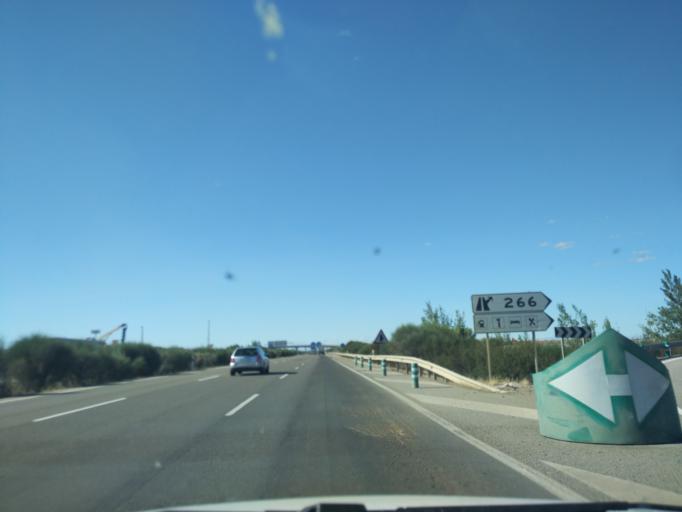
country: ES
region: Castille and Leon
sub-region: Provincia de Zamora
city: Benavente
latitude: 42.0352
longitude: -5.6719
